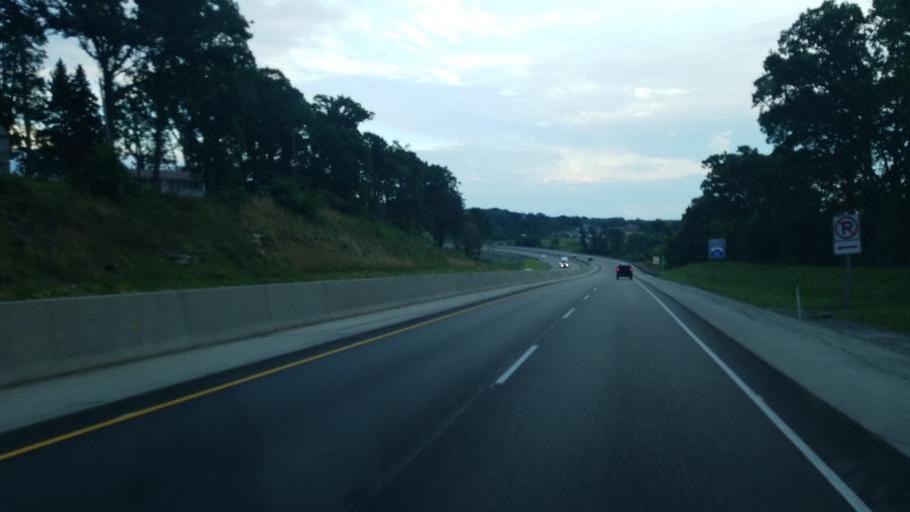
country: US
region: Pennsylvania
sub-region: Somerset County
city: Somerset
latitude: 40.0119
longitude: -79.0710
